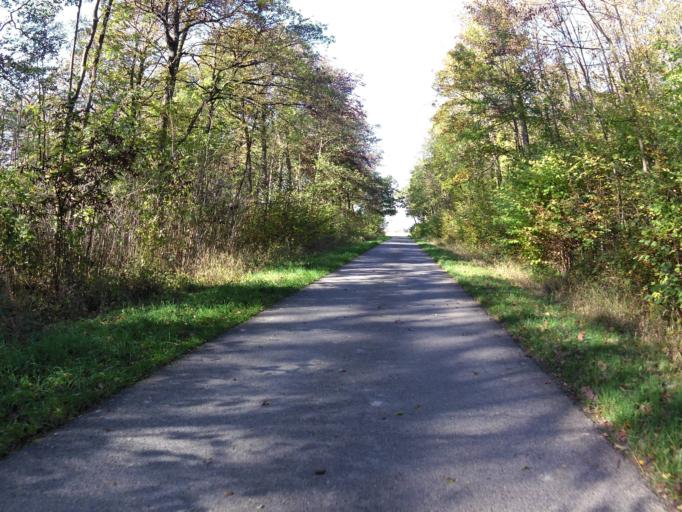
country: DE
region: Bavaria
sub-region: Regierungsbezirk Unterfranken
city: Sulzfeld am Main
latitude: 49.7208
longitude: 10.0988
